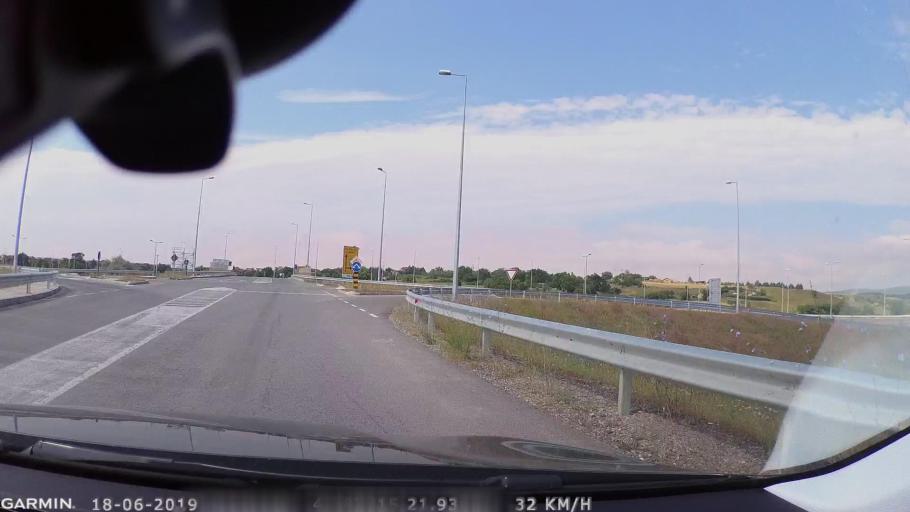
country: MK
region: Sveti Nikole
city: Sveti Nikole
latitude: 41.8782
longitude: 21.9388
